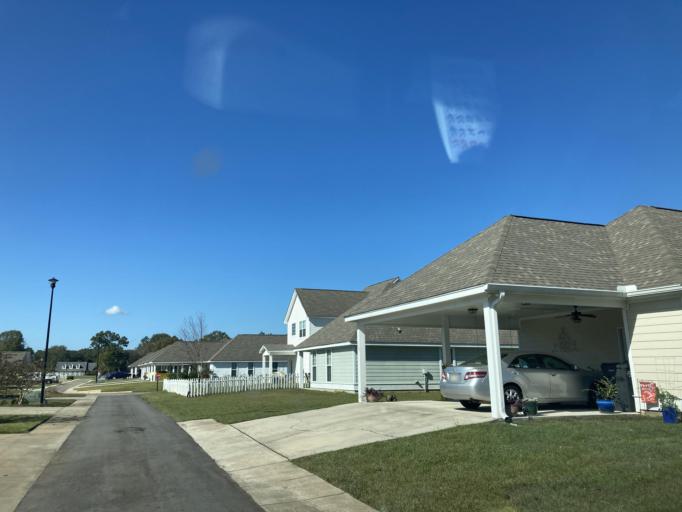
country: US
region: Mississippi
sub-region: Lamar County
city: West Hattiesburg
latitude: 31.2821
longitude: -89.4129
